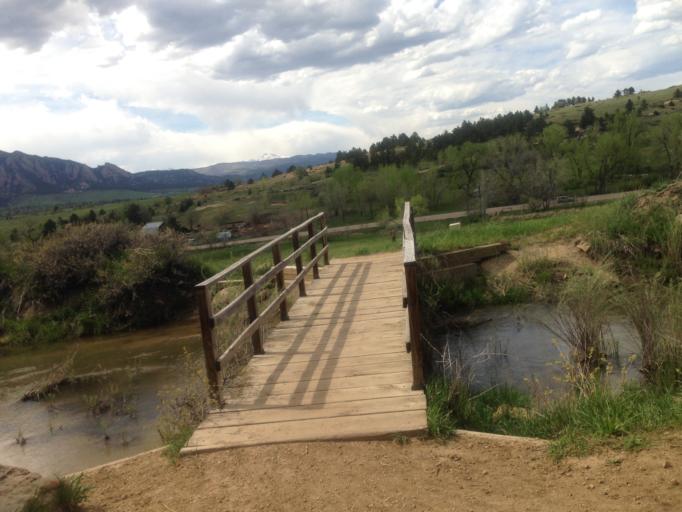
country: US
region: Colorado
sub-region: Boulder County
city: Superior
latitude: 39.9543
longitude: -105.2176
